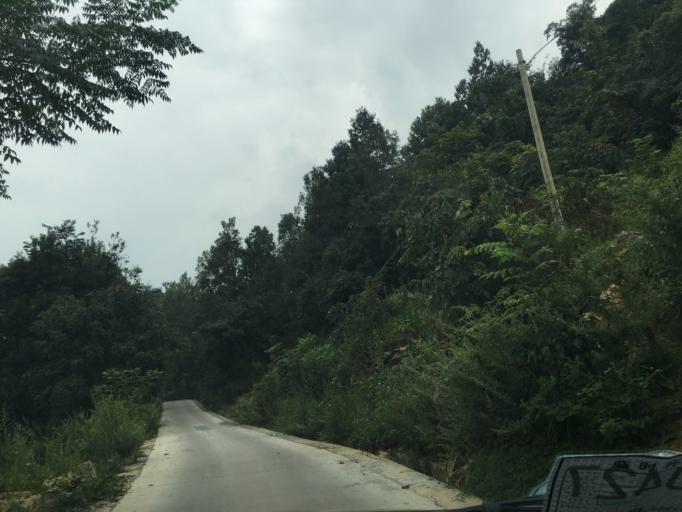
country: CN
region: Guangxi Zhuangzu Zizhiqu
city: Xinzhou
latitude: 25.5645
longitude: 105.6028
